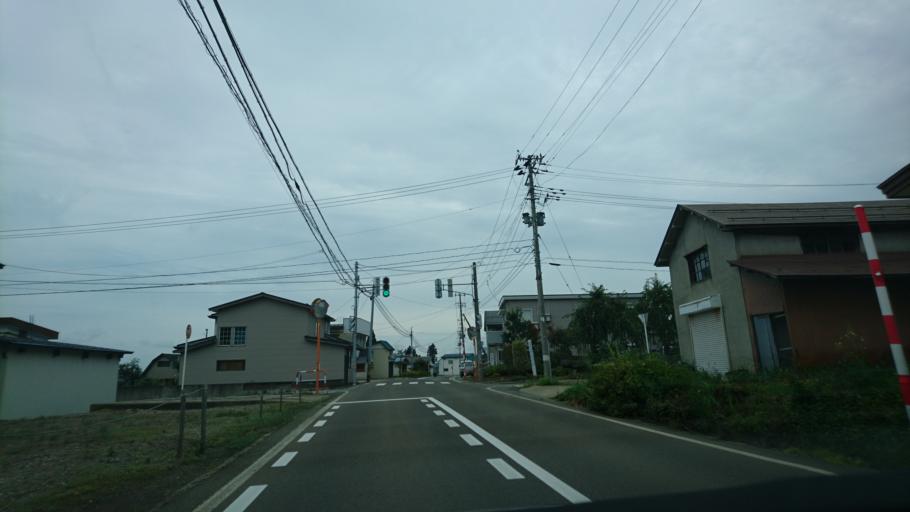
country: JP
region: Akita
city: Yuzawa
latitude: 39.1438
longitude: 140.5759
